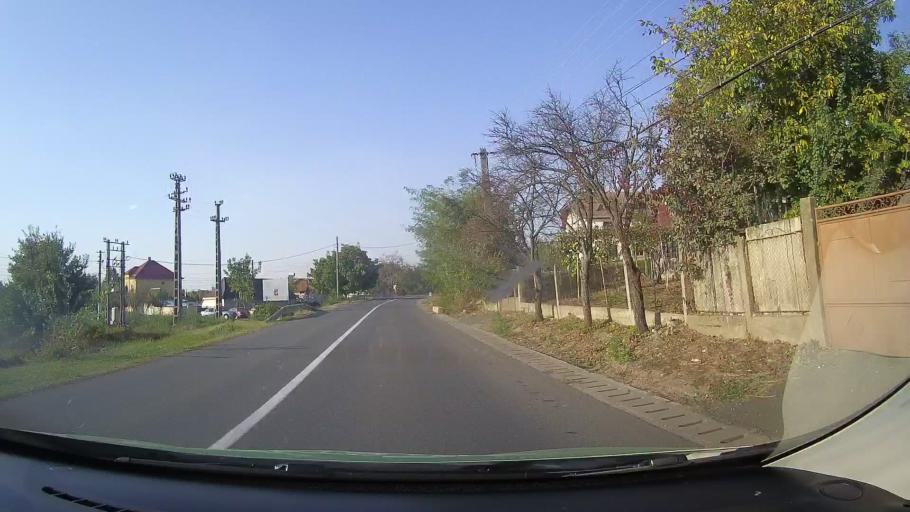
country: RO
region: Arad
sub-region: Comuna Ghioroc
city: Cuvin
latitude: 46.1612
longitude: 21.5919
